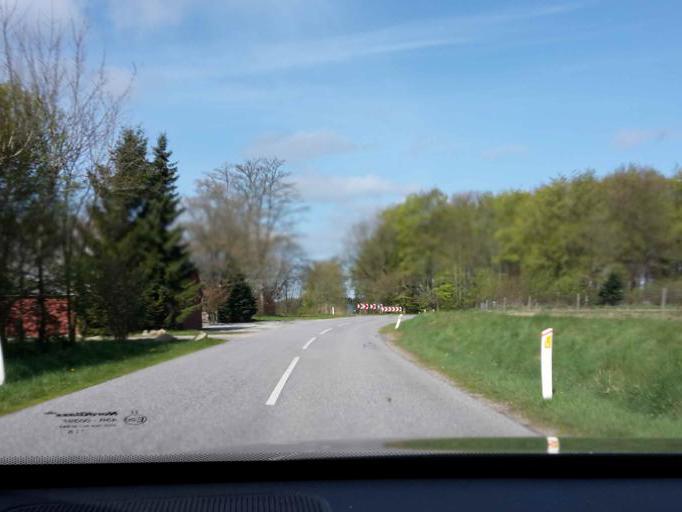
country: DK
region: South Denmark
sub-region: Vejen Kommune
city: Holsted
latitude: 55.5893
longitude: 8.9444
